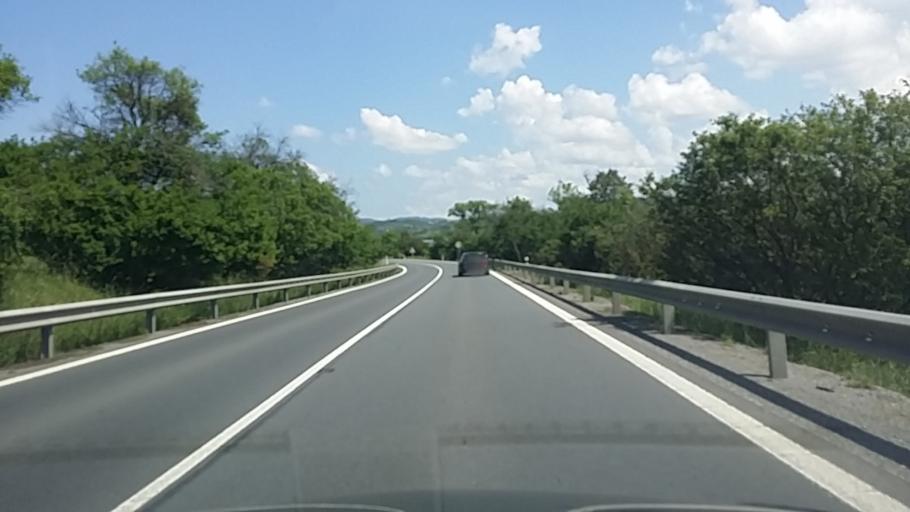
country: SK
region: Banskobystricky
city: Krupina
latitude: 48.3226
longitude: 19.0575
